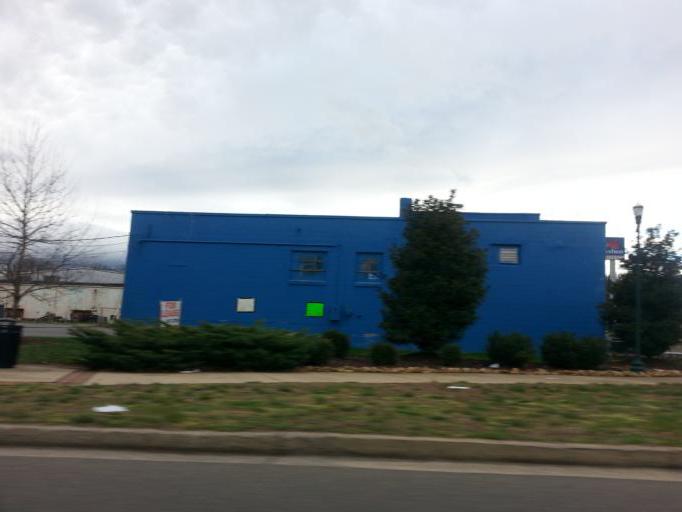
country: US
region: Tennessee
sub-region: Washington County
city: Johnson City
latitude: 36.3128
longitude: -82.3552
